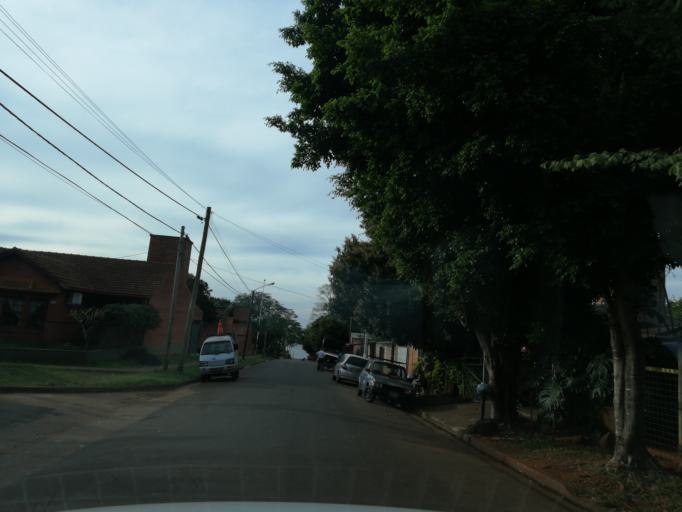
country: AR
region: Misiones
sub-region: Departamento de Capital
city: Posadas
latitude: -27.3577
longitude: -55.9191
